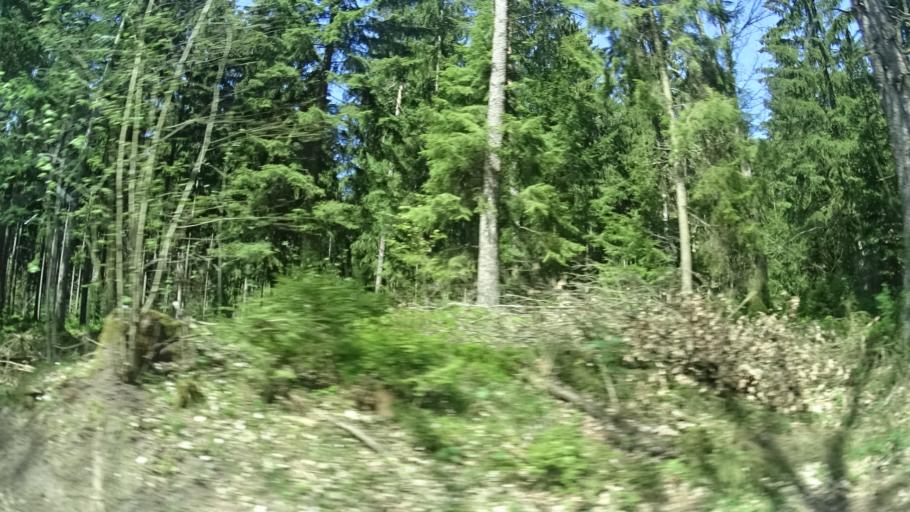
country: DE
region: Thuringia
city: Hildburghausen
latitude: 50.4475
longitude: 10.7669
